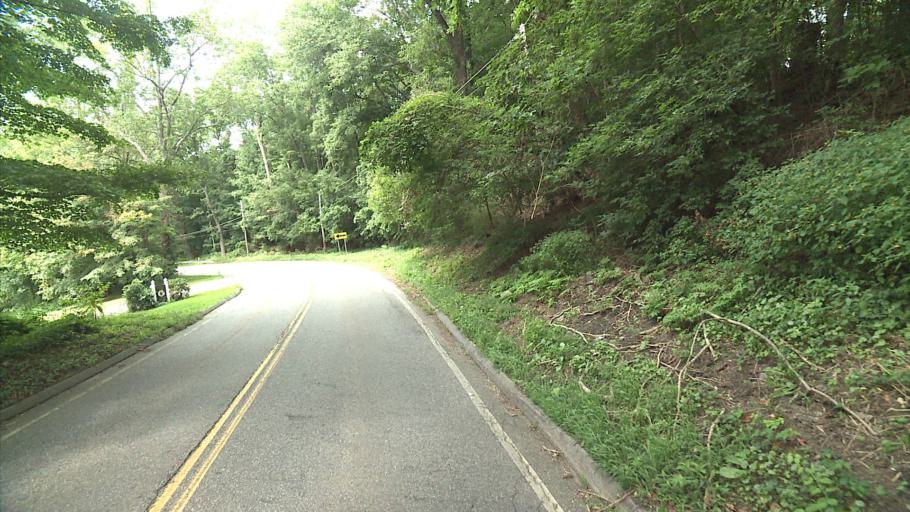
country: US
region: Connecticut
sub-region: Windham County
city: South Windham
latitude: 41.6467
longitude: -72.1940
